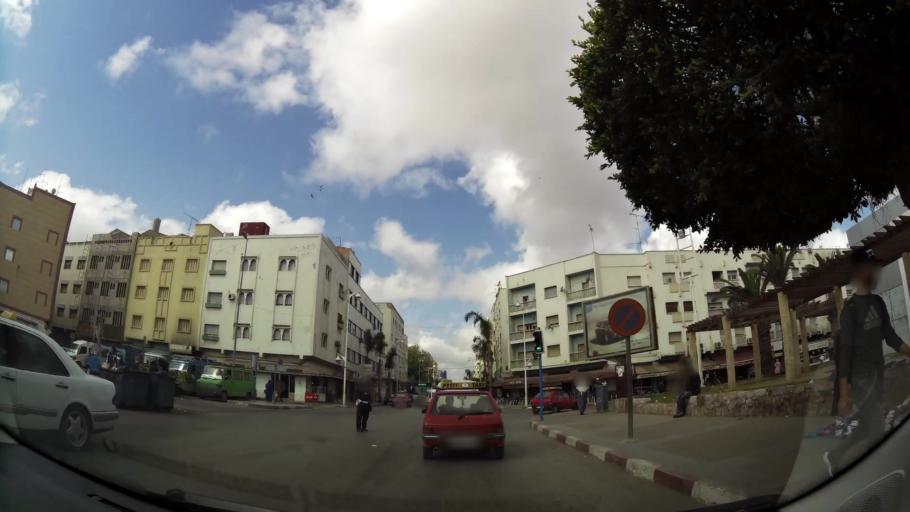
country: MA
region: Oriental
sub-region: Nador
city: Nador
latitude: 35.1747
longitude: -2.9218
